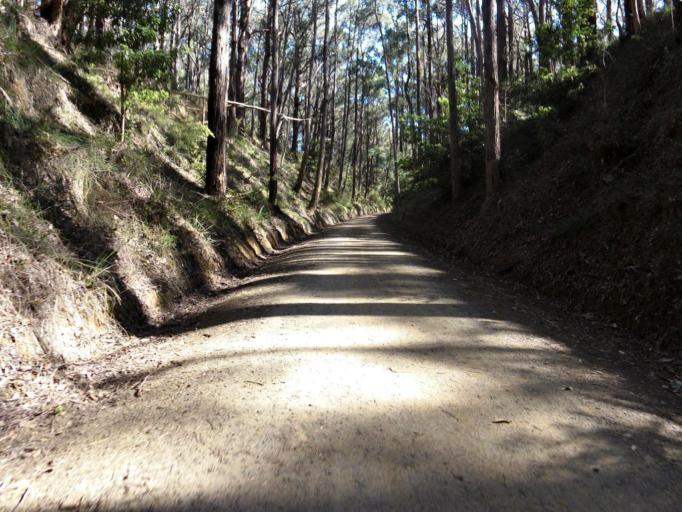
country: AU
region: Victoria
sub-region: Latrobe
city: Moe
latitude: -38.3981
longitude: 146.1748
